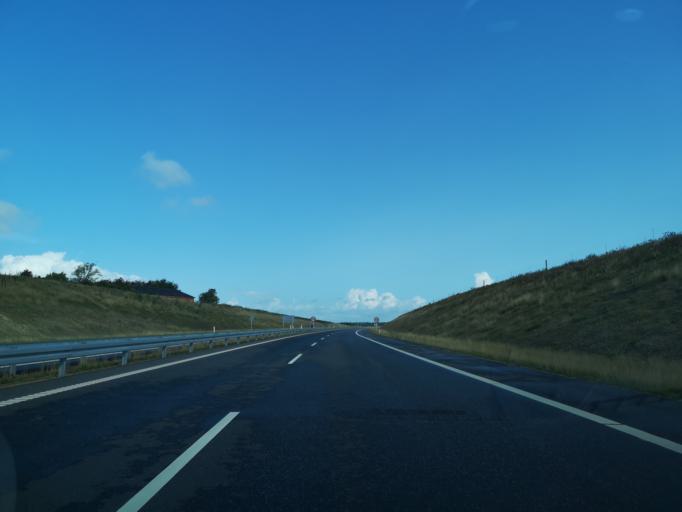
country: DK
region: Central Jutland
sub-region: Herning Kommune
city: Snejbjerg
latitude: 56.1346
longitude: 8.8705
